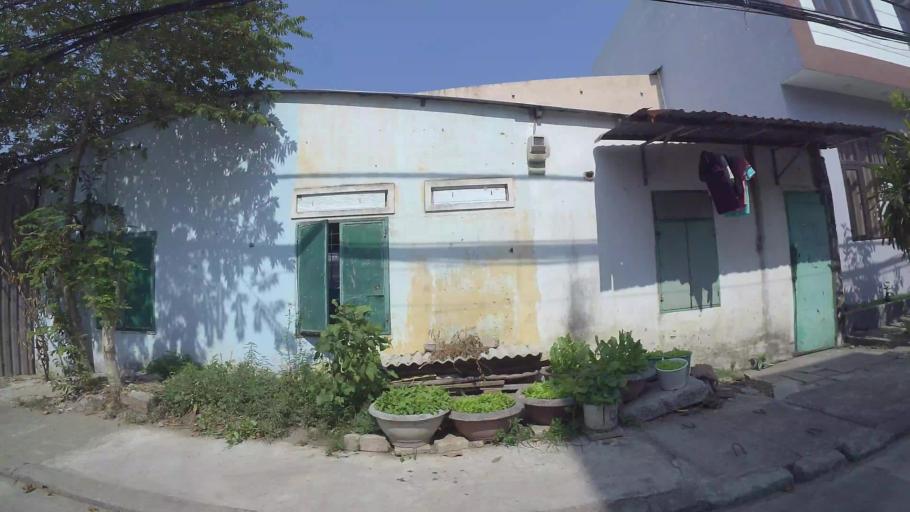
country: VN
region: Da Nang
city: Ngu Hanh Son
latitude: 16.0227
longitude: 108.2516
